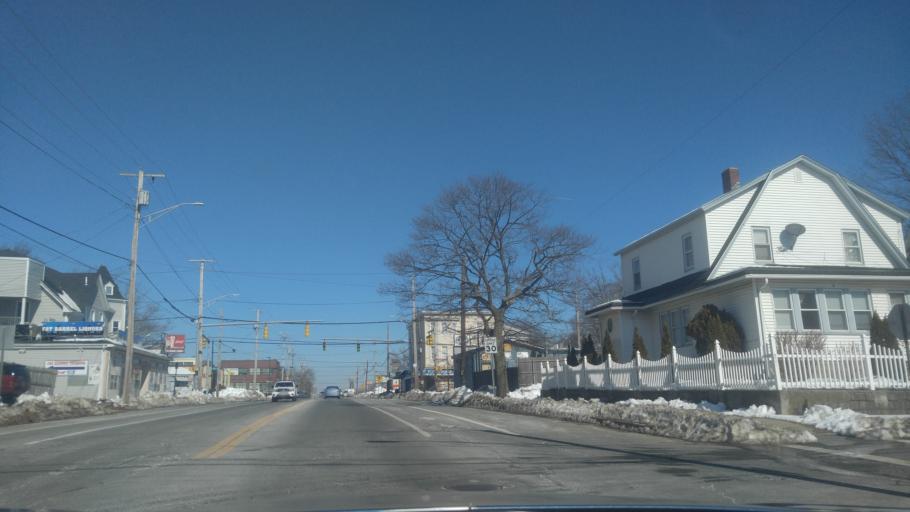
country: US
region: Rhode Island
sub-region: Providence County
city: East Providence
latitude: 41.7904
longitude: -71.3964
